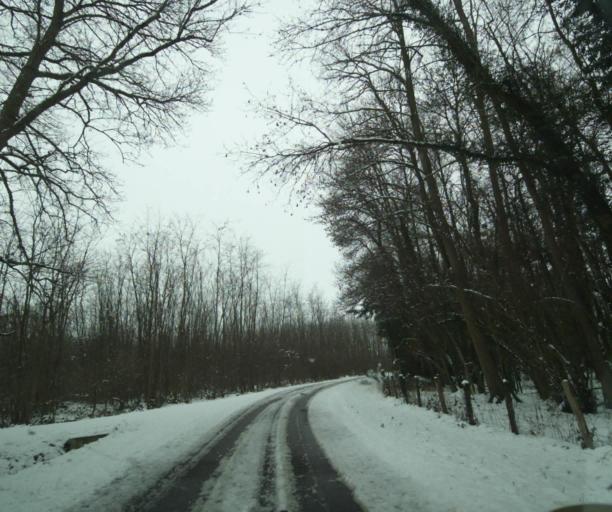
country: FR
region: Champagne-Ardenne
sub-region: Departement de la Haute-Marne
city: Montier-en-Der
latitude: 48.4660
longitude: 4.6557
